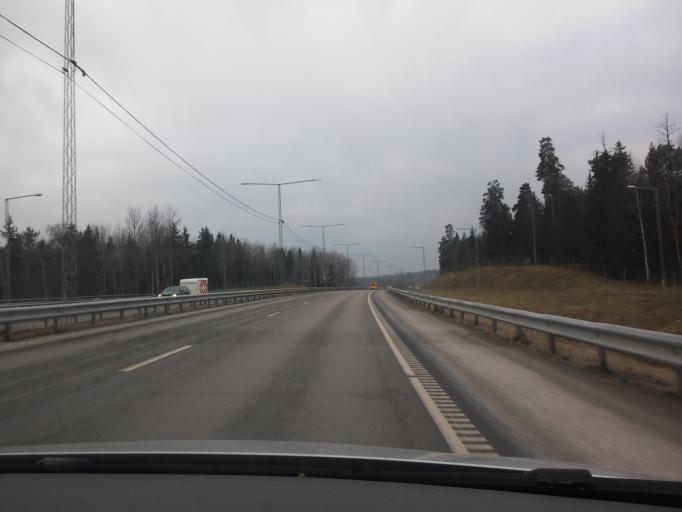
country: SE
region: Stockholm
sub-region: Taby Kommun
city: Taby
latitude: 59.4644
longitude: 18.1483
